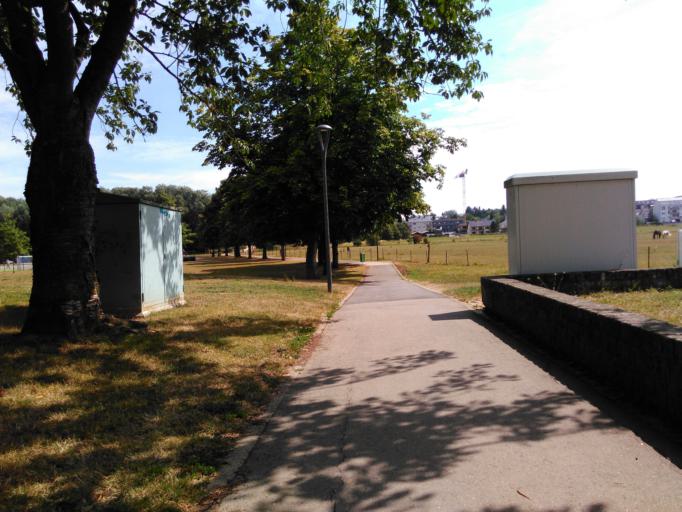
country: LU
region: Luxembourg
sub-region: Canton de Luxembourg
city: Hesperange
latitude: 49.5688
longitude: 6.1548
